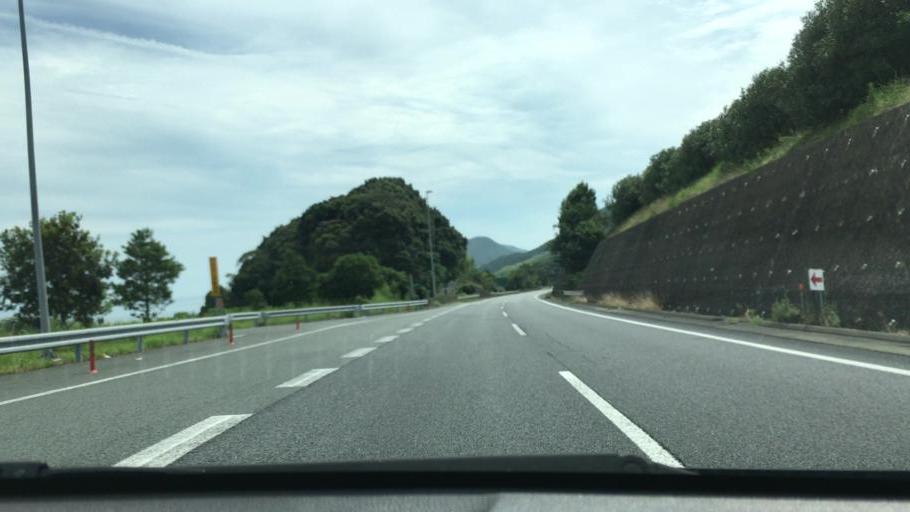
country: JP
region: Yamaguchi
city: Hofu
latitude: 34.0603
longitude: 131.6517
